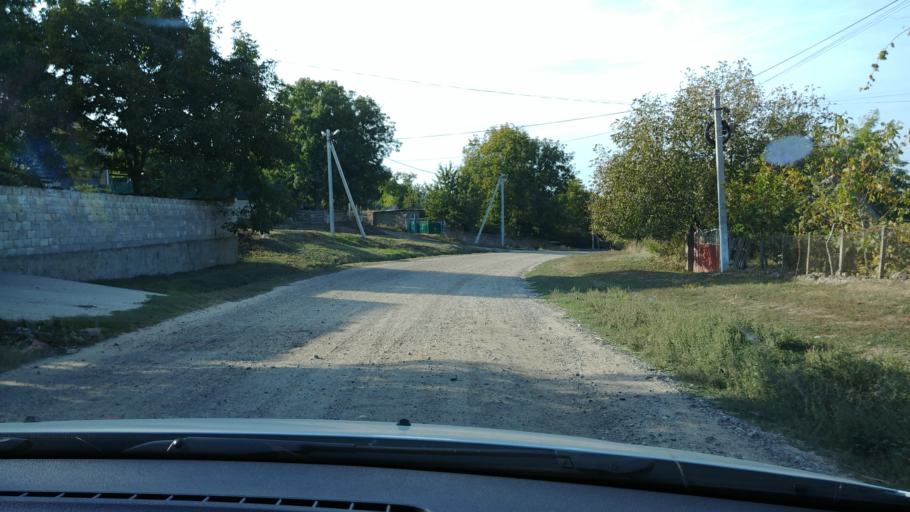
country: MD
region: Rezina
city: Rezina
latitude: 47.7474
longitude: 28.8854
